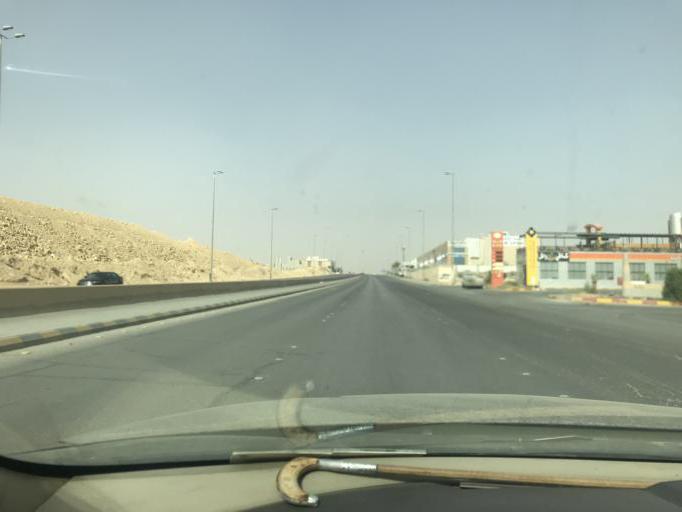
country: SA
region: Ar Riyad
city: Riyadh
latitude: 24.8146
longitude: 46.6803
